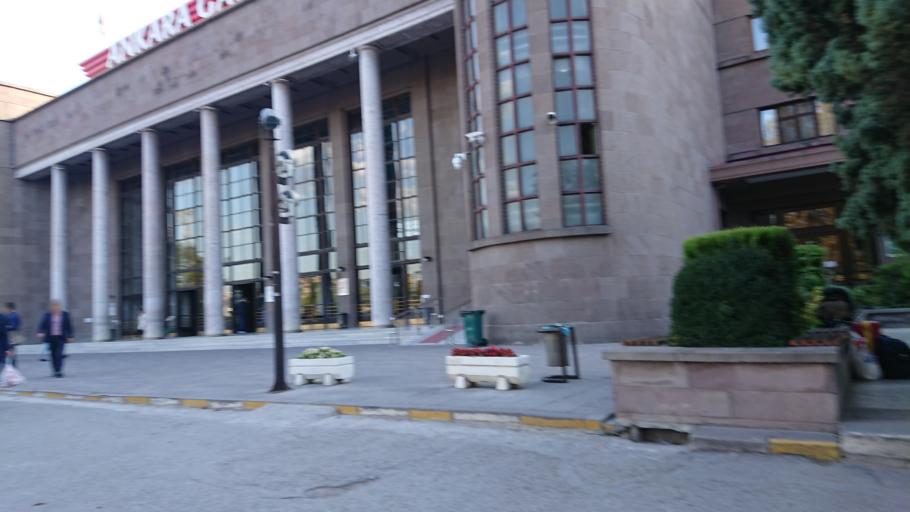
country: TR
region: Ankara
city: Ankara
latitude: 39.9366
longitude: 32.8437
